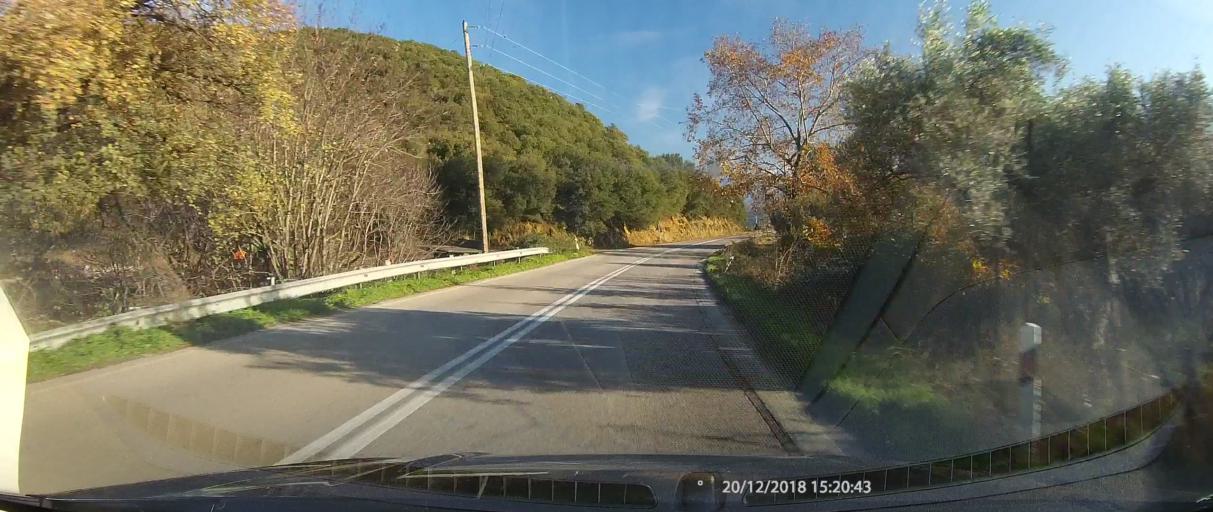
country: GR
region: Central Greece
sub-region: Nomos Fthiotidos
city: Makrakomi
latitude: 38.9336
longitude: 22.0623
